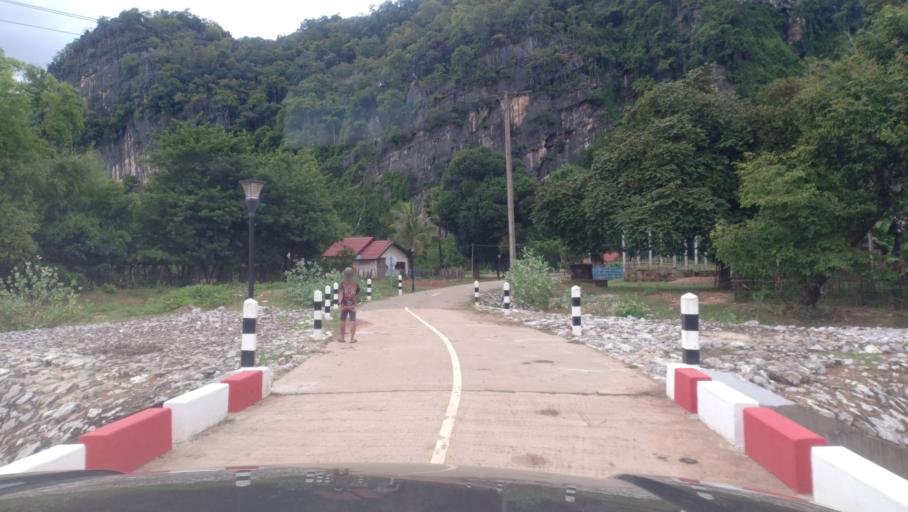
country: LA
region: Khammouan
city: Thakhek
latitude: 17.4290
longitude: 104.8638
